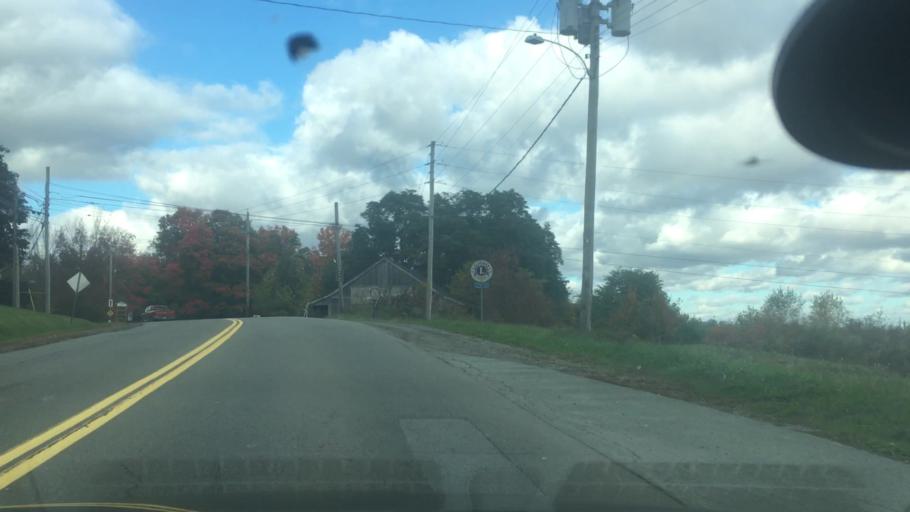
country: CA
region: Nova Scotia
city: Windsor
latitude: 44.9775
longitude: -64.1223
